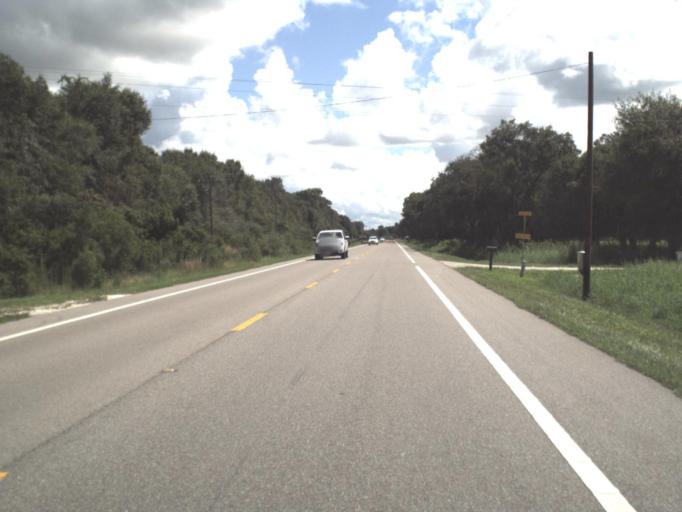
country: US
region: Florida
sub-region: Sarasota County
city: Lake Sarasota
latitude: 27.3570
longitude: -82.1833
